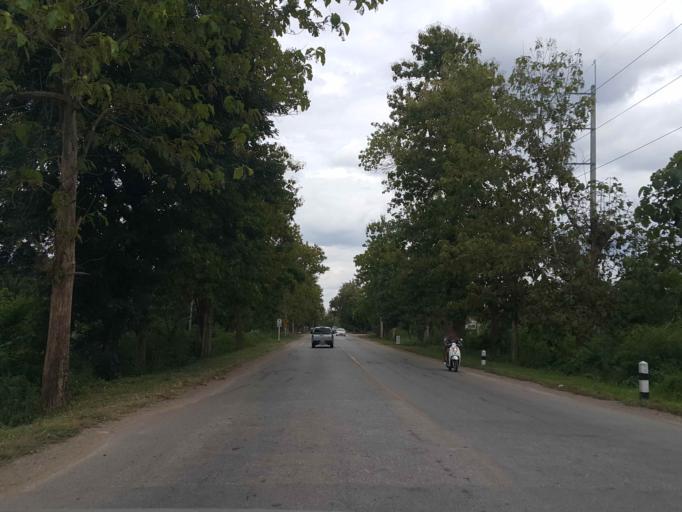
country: TH
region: Chiang Mai
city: Doi Lo
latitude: 18.4328
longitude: 98.8695
